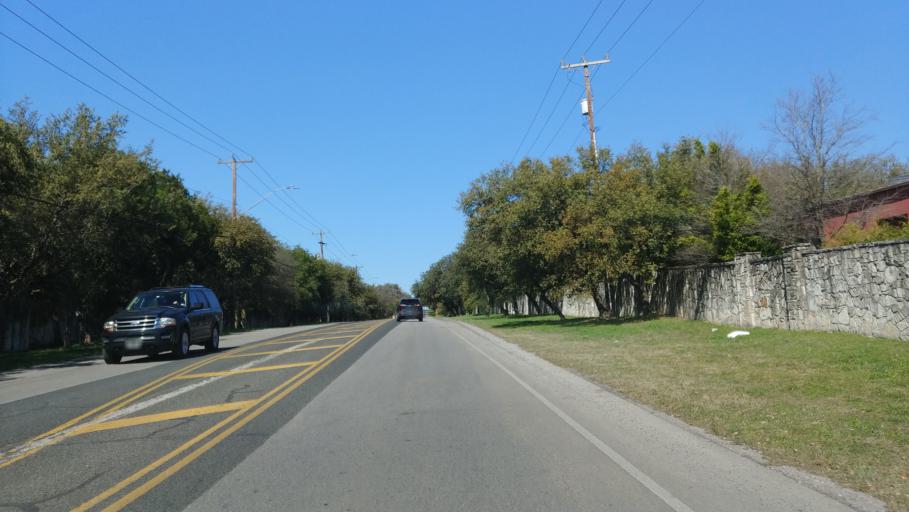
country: US
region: Texas
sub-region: Bexar County
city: Shavano Park
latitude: 29.5598
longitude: -98.5521
